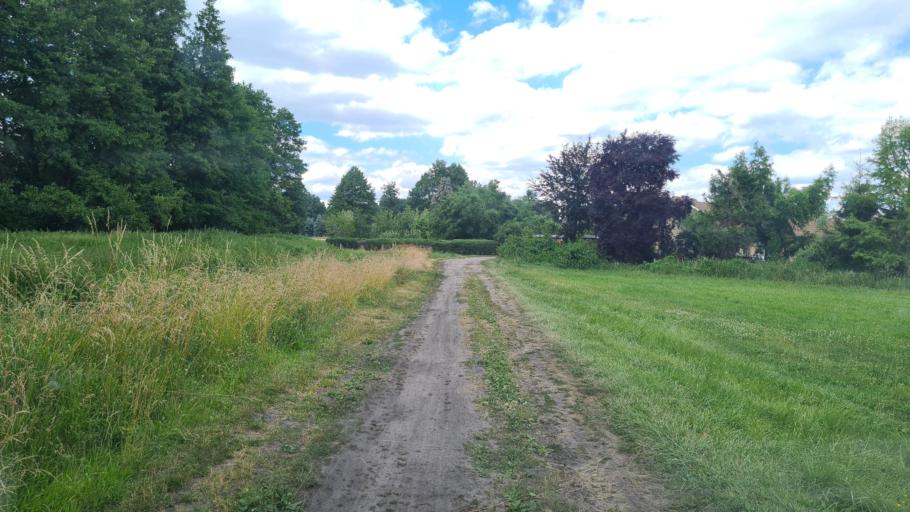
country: DE
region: Brandenburg
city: Luckenwalde
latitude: 52.1083
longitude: 13.2059
